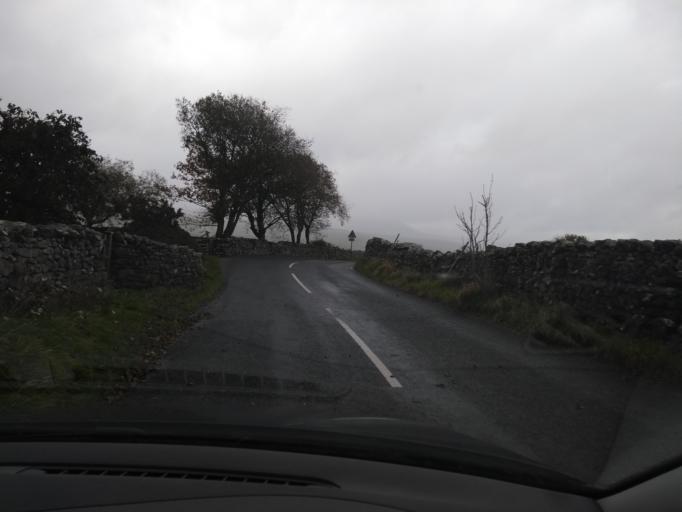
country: GB
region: England
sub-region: North Yorkshire
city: Settle
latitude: 54.1772
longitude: -2.3338
